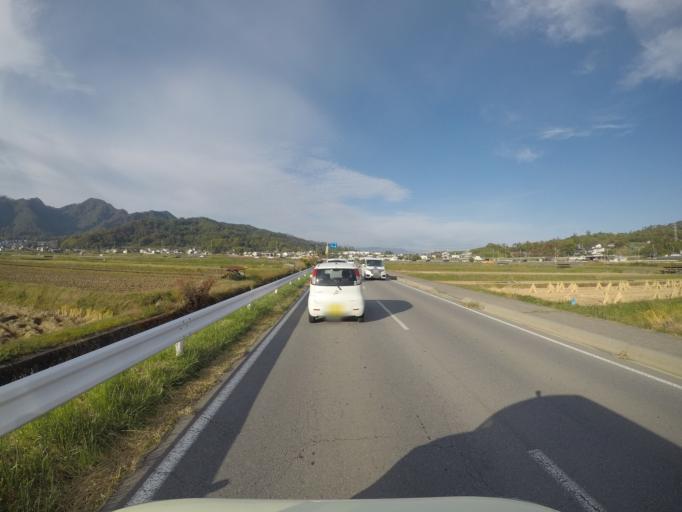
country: JP
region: Nagano
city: Kamimaruko
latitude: 36.3456
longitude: 138.2661
